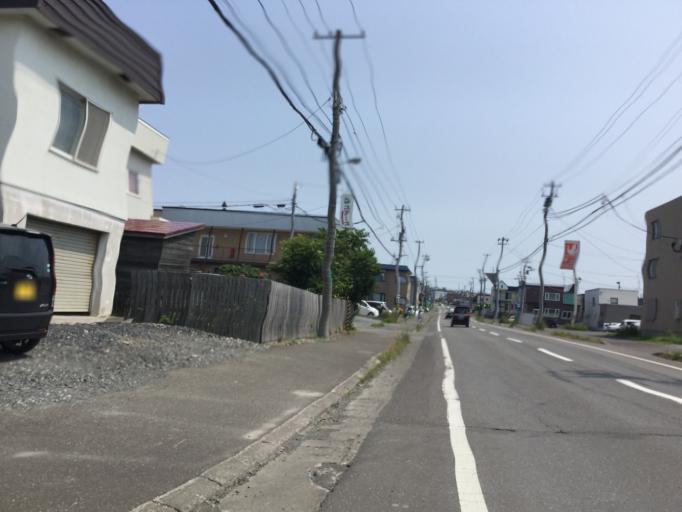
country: JP
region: Hokkaido
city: Wakkanai
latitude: 45.3864
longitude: 141.7121
